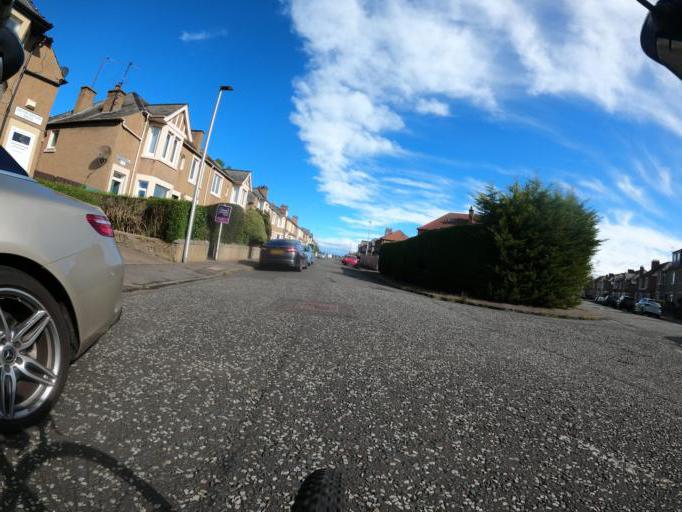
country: GB
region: Scotland
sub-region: Edinburgh
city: Edinburgh
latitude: 55.9656
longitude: -3.2422
